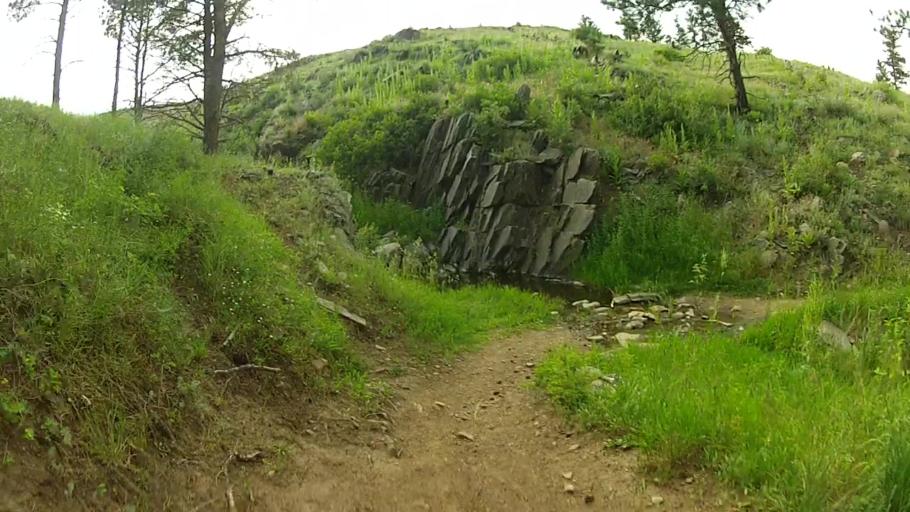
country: US
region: Colorado
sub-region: Larimer County
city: Laporte
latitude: 40.4772
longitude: -105.2356
